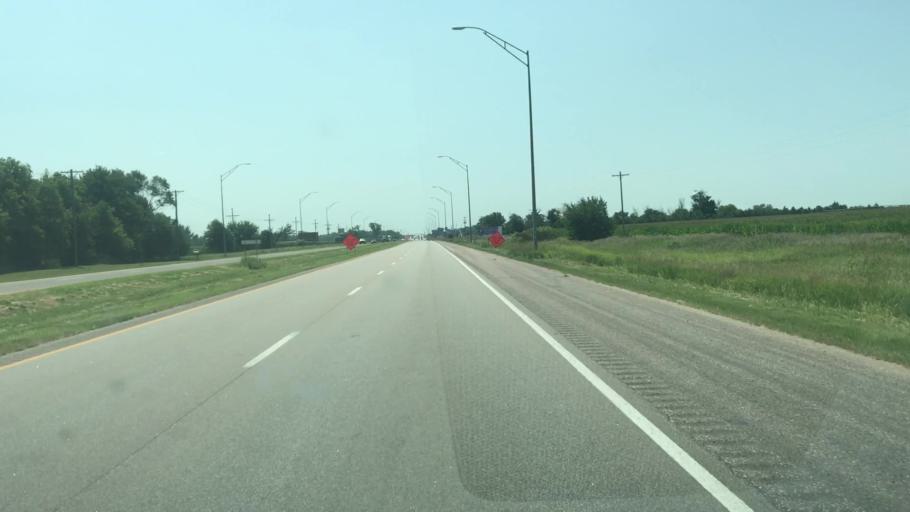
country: US
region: Nebraska
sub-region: Hall County
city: Grand Island
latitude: 40.8438
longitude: -98.3787
